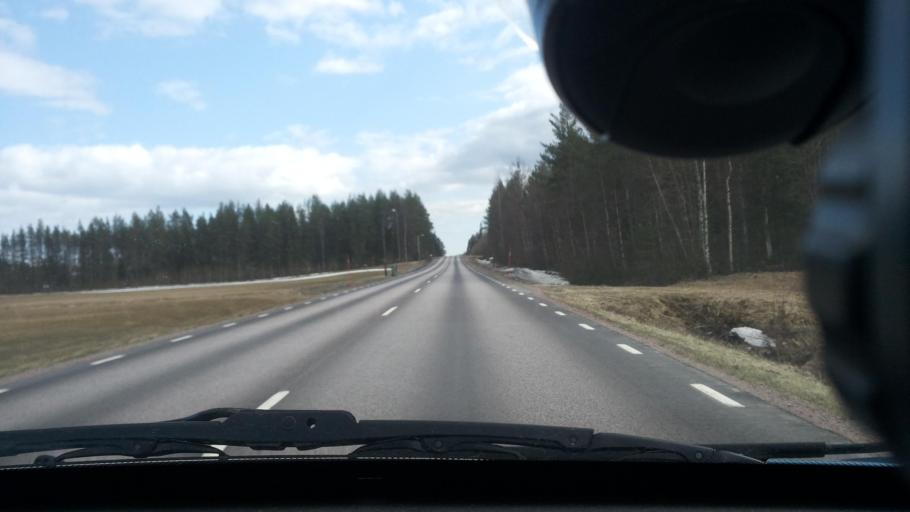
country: SE
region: Norrbotten
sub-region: Lulea Kommun
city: Sodra Sunderbyn
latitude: 65.6213
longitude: 21.9399
